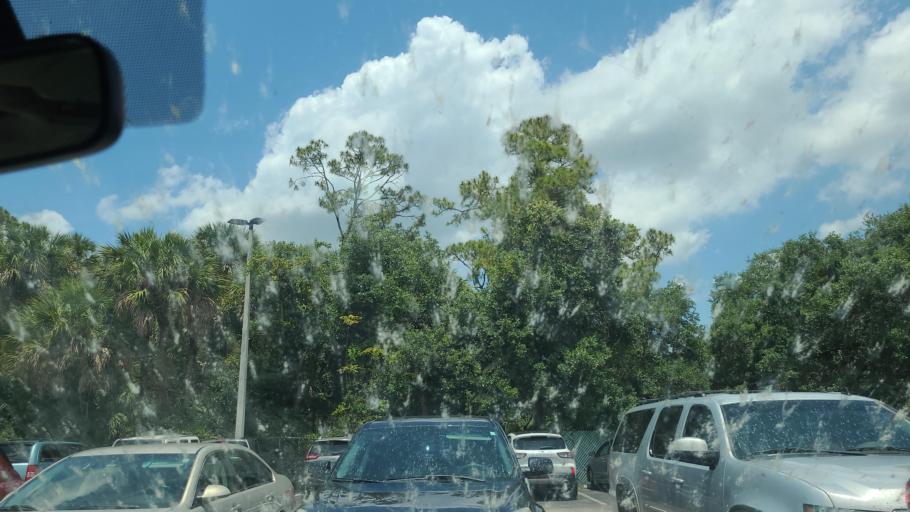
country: US
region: Florida
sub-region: Glades County
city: Buckhead Ridge
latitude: 27.0882
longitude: -81.0717
